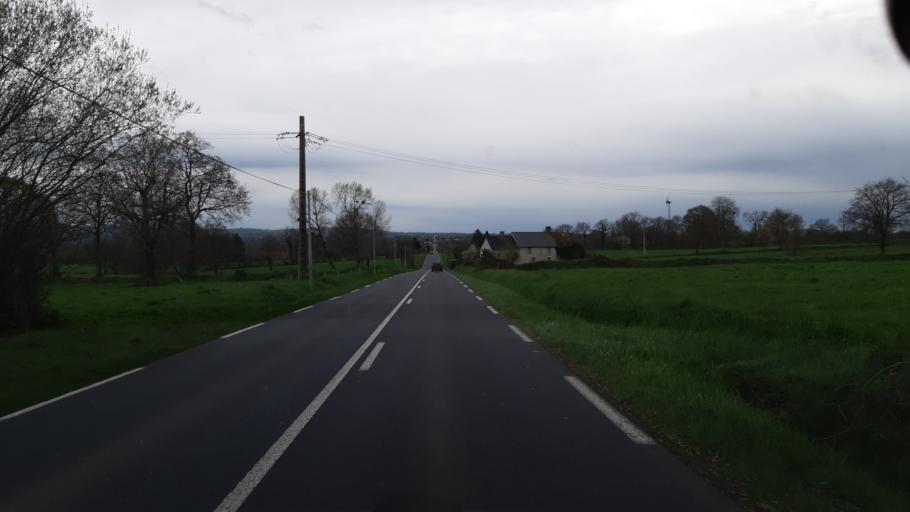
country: FR
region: Lower Normandy
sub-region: Departement de la Manche
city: Tessy-sur-Vire
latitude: 49.0148
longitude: -1.1489
